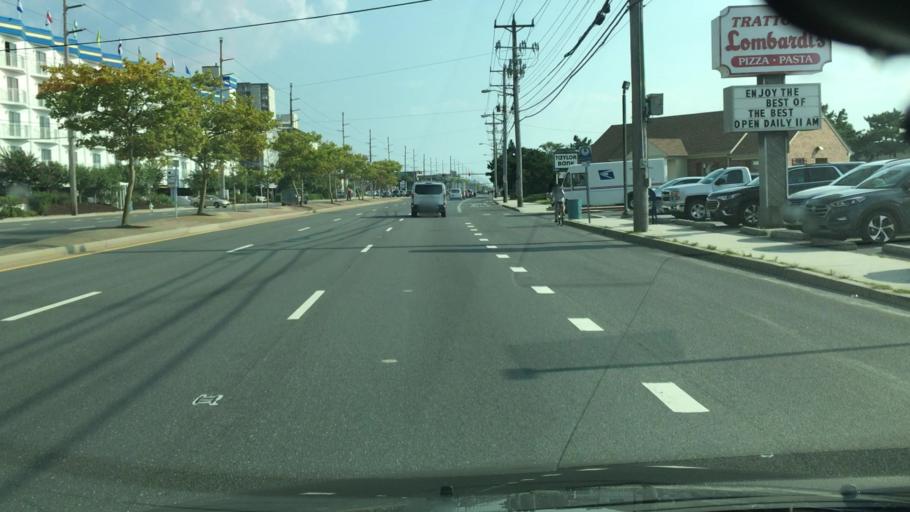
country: US
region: Maryland
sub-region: Worcester County
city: Ocean City
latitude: 38.4084
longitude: -75.0590
